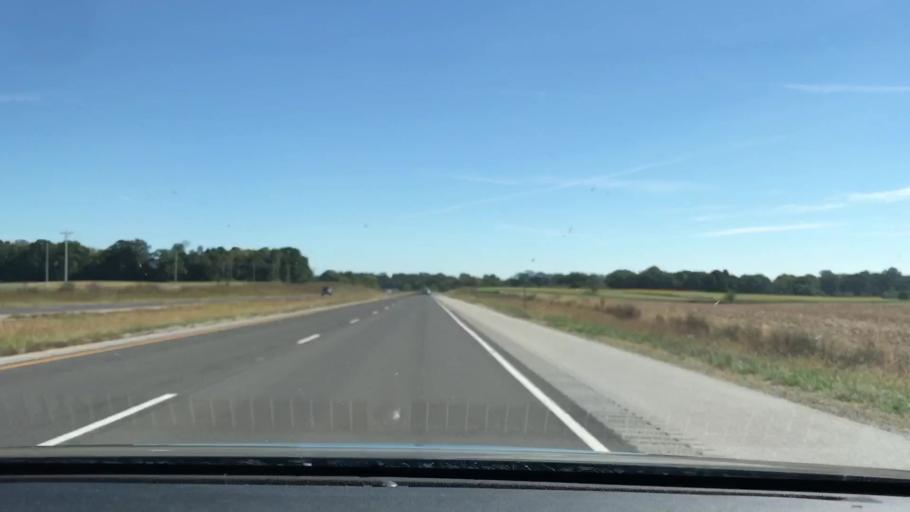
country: US
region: Kentucky
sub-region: Todd County
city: Elkton
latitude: 36.8136
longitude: -87.0210
